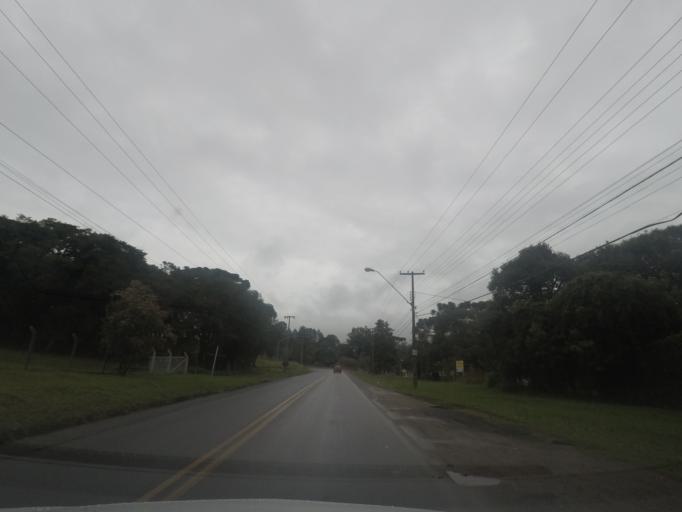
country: BR
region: Parana
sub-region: Campina Grande Do Sul
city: Campina Grande do Sul
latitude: -25.3231
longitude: -49.0780
